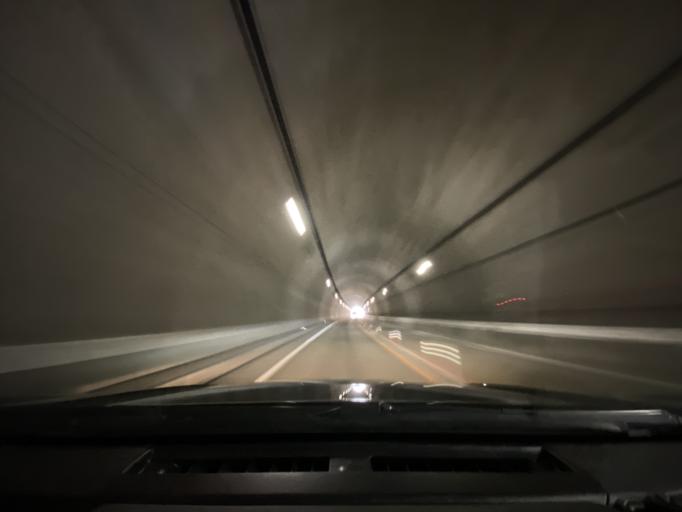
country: JP
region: Hokkaido
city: Shimo-furano
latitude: 42.9735
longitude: 142.3861
